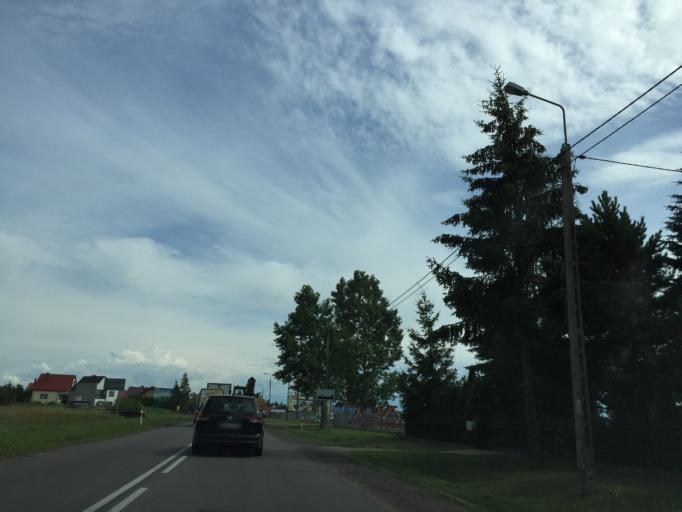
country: PL
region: Podlasie
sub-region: Powiat siemiatycki
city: Siemiatycze
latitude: 52.4404
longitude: 22.8511
